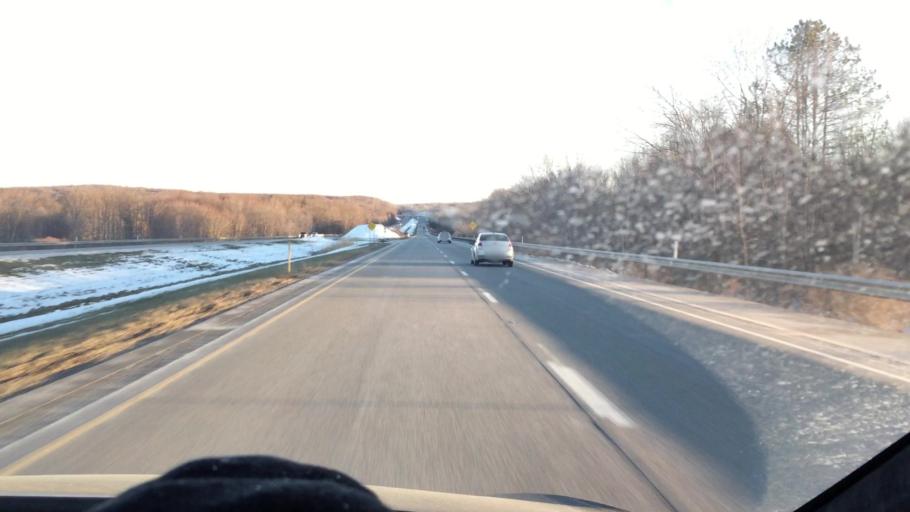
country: US
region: Pennsylvania
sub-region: Crawford County
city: Meadville
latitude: 41.6656
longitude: -80.2081
